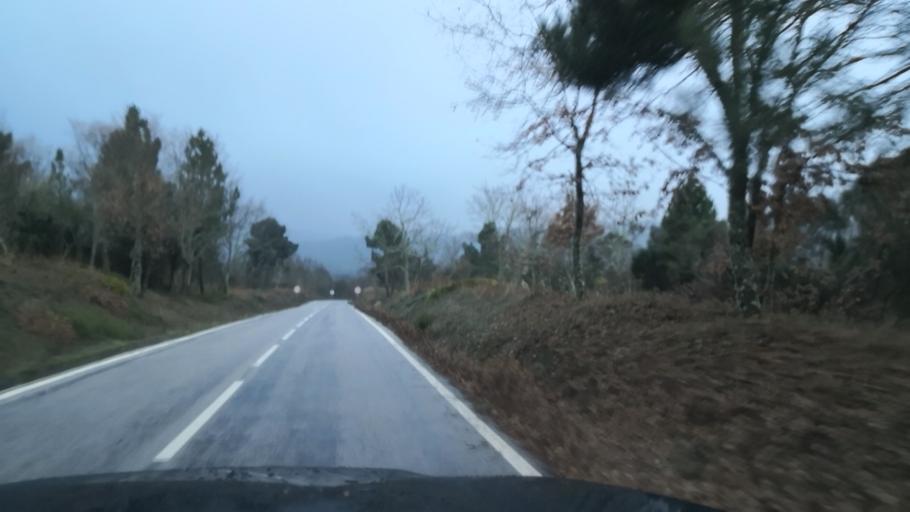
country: PT
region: Vila Real
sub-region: Murca
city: Murca
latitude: 41.4386
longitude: -7.5336
